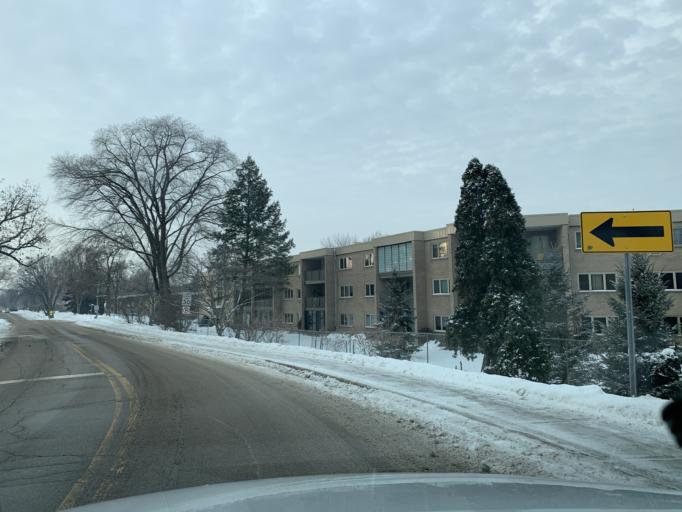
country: US
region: Minnesota
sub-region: Hennepin County
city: Saint Louis Park
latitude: 44.9206
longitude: -93.3538
